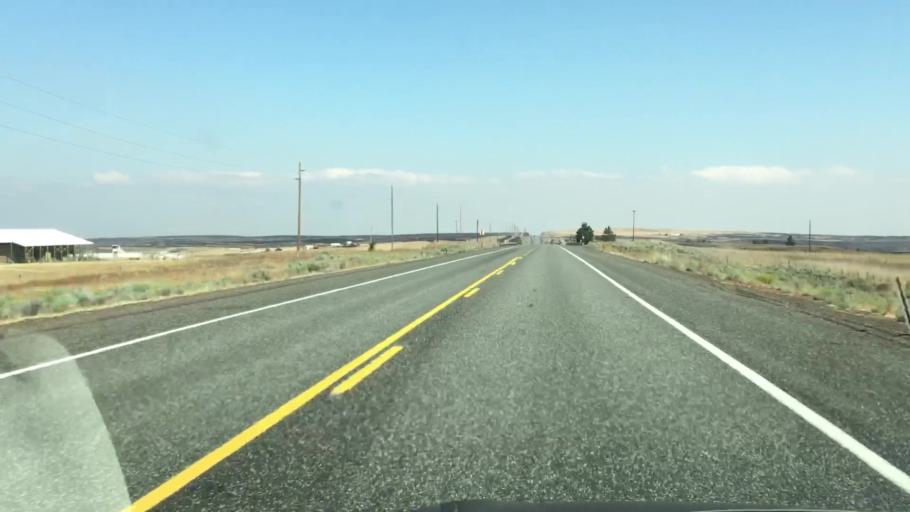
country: US
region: Oregon
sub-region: Wasco County
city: The Dalles
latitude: 45.3403
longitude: -121.1422
